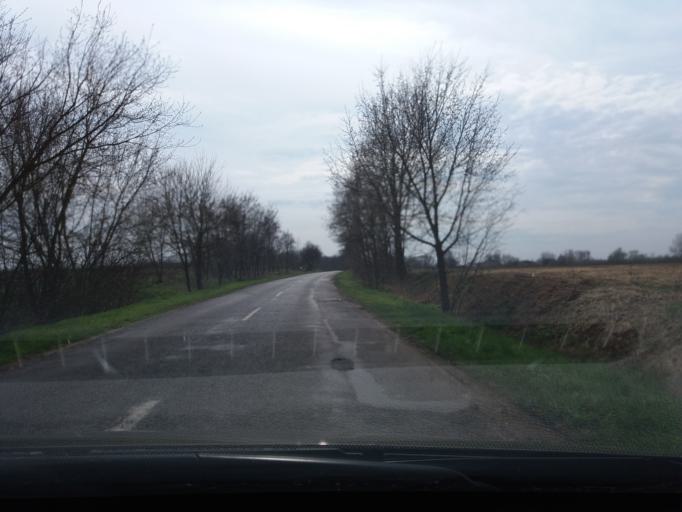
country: HU
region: Szabolcs-Szatmar-Bereg
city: Petnehaza
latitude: 48.0746
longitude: 22.0890
